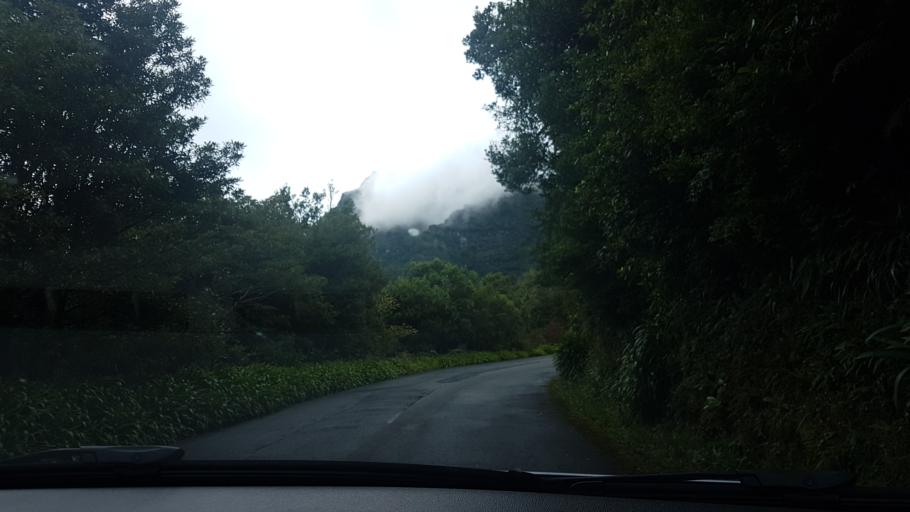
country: PT
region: Madeira
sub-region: Sao Vicente
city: Sao Vicente
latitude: 32.7588
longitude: -17.0169
